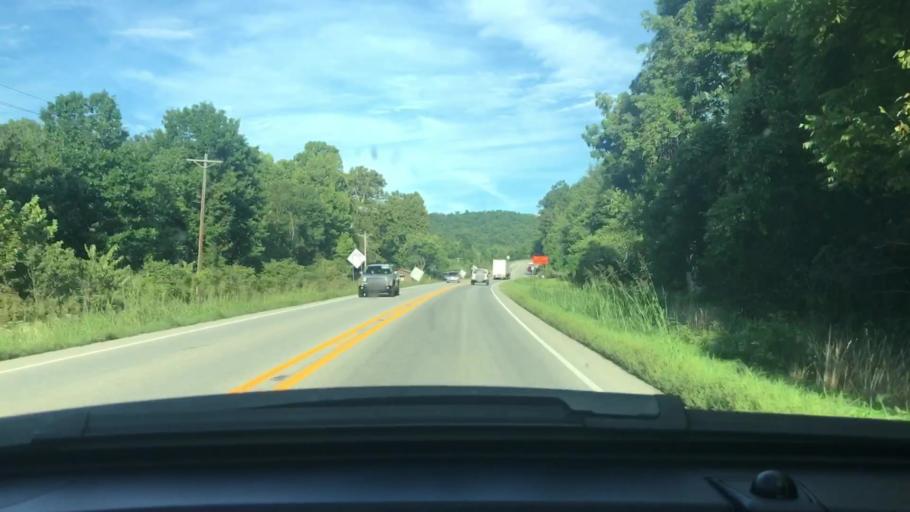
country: US
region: Arkansas
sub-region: Sharp County
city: Cherokee Village
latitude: 36.3036
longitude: -91.4234
